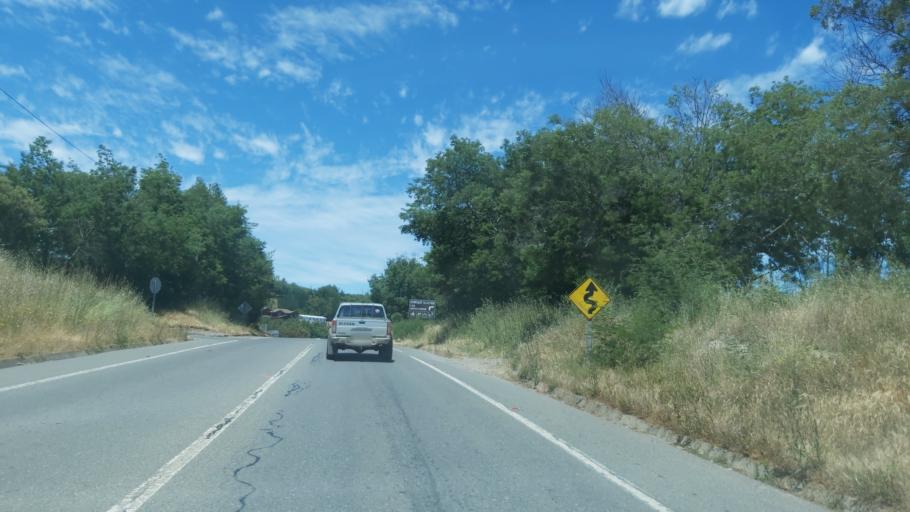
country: CL
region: Maule
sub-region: Provincia de Talca
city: Constitucion
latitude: -35.3268
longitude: -72.3854
